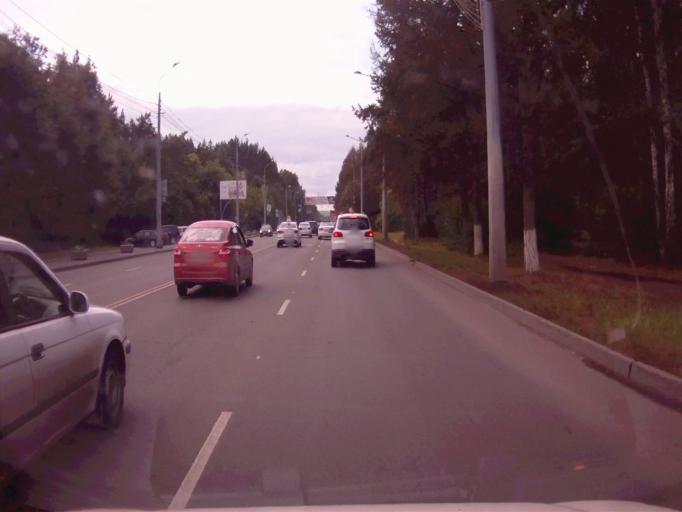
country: RU
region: Chelyabinsk
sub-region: Gorod Chelyabinsk
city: Chelyabinsk
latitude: 55.1472
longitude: 61.3554
